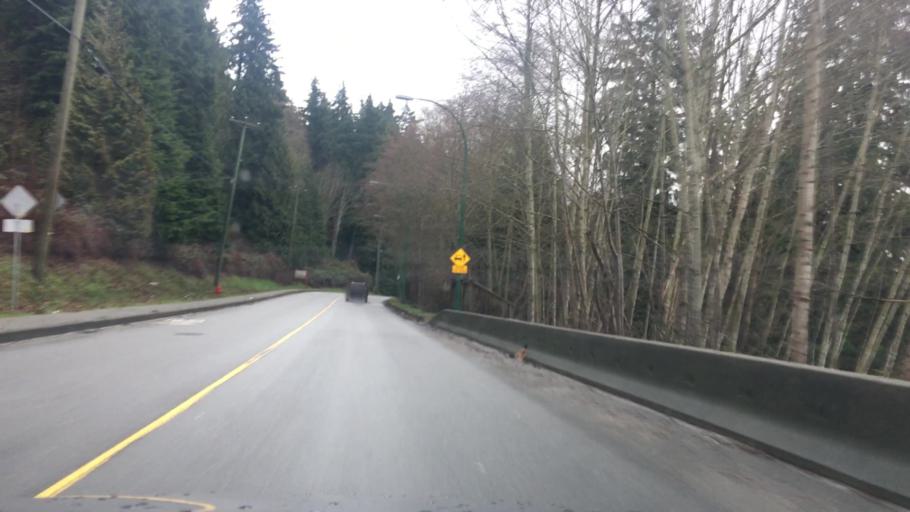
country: CA
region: British Columbia
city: Burnaby
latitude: 49.3078
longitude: -122.9823
